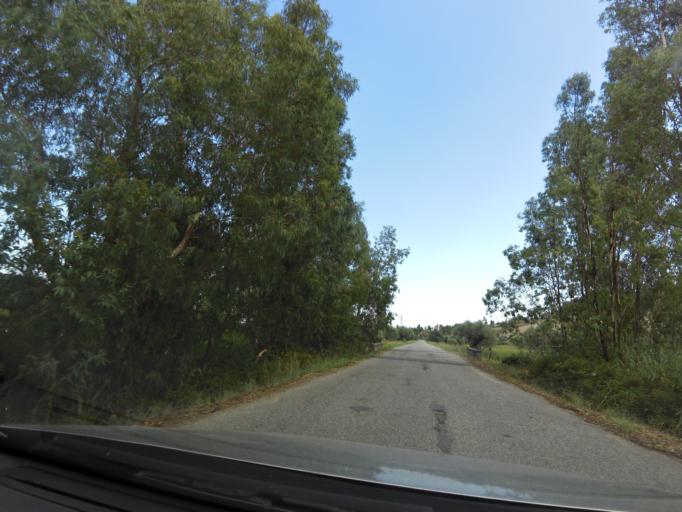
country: IT
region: Calabria
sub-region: Provincia di Reggio Calabria
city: Monasterace
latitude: 38.4273
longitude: 16.5301
